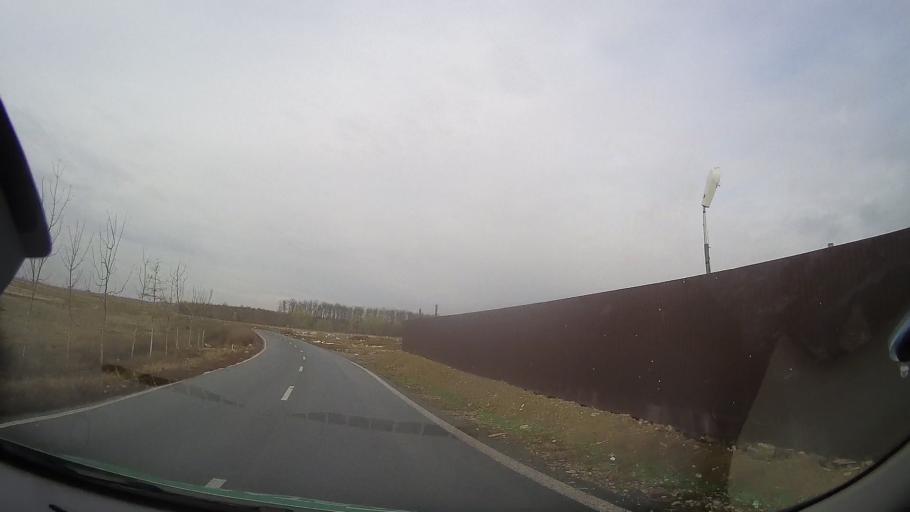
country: RO
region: Ialomita
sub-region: Comuna Fierbinti-Targ
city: Fierbinti-Targ
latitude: 44.6744
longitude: 26.3506
